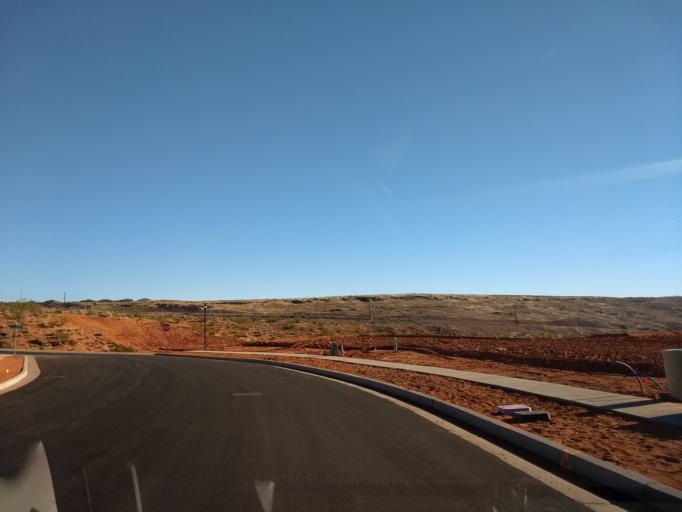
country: US
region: Utah
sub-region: Washington County
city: Washington
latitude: 37.1411
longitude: -113.4804
